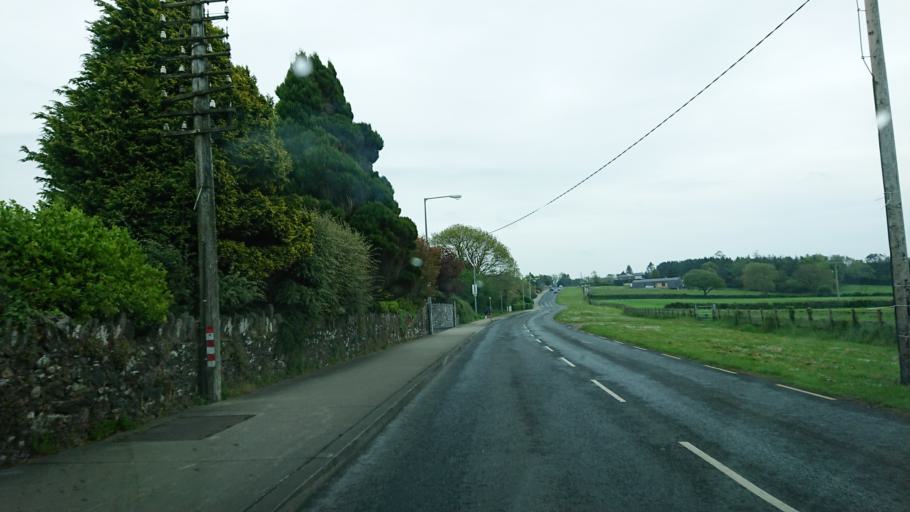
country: IE
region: Munster
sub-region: Waterford
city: Waterford
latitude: 52.2395
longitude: -7.0860
